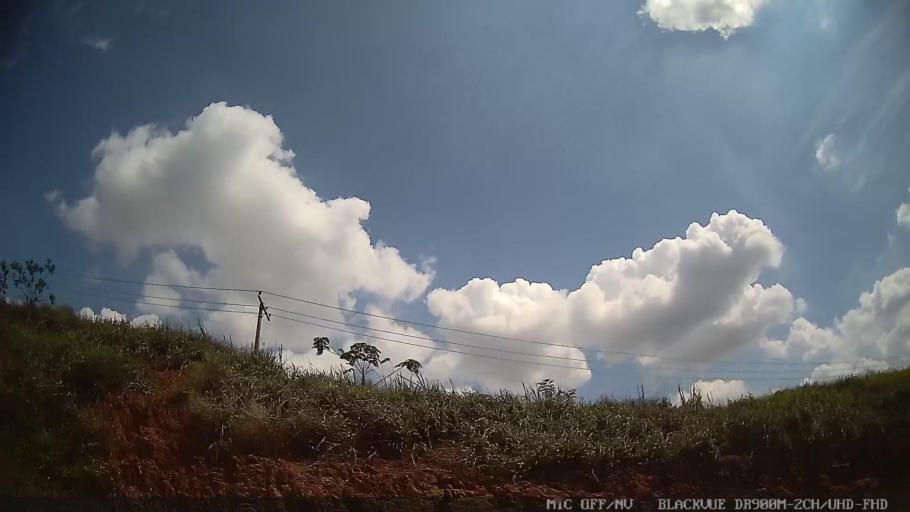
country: BR
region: Sao Paulo
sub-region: Itatiba
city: Itatiba
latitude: -22.9806
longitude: -46.7796
